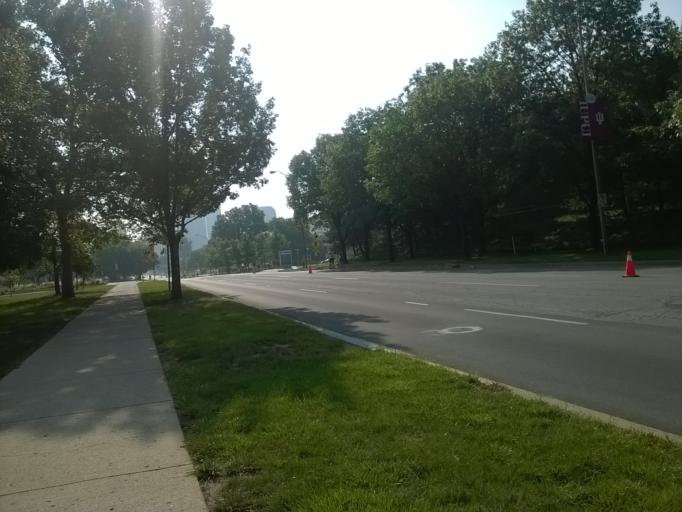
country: US
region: Indiana
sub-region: Marion County
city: Indianapolis
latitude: 39.7718
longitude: -86.1744
